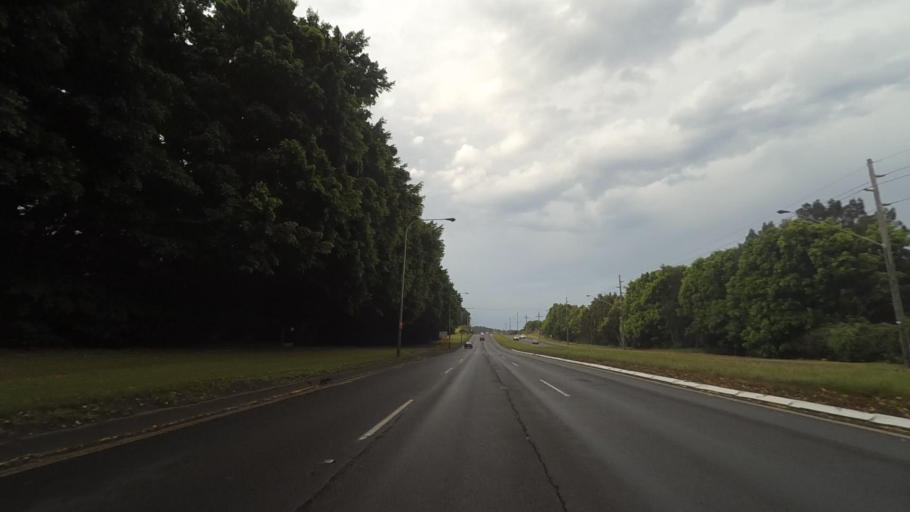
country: AU
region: New South Wales
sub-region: Wollongong
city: Coniston
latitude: -34.4537
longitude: 150.8738
